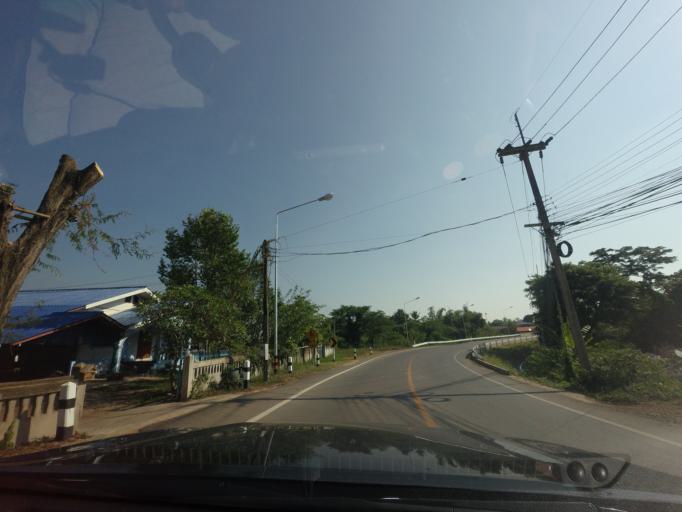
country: TH
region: Nan
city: Nan
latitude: 18.7882
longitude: 100.7925
